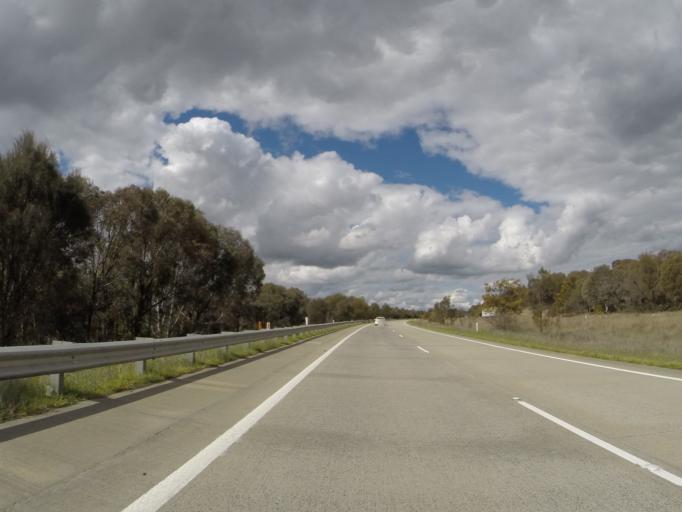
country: AU
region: New South Wales
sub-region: Yass Valley
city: Gundaroo
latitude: -34.7877
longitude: 149.2028
